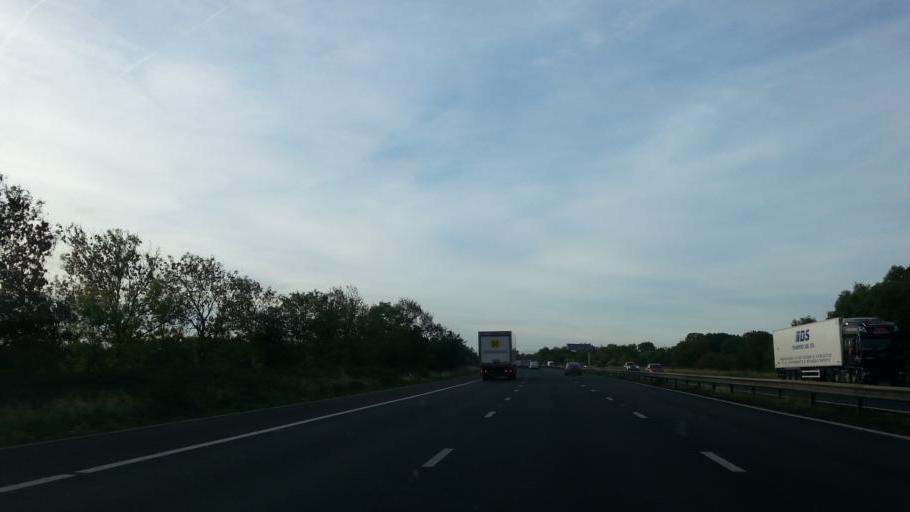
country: GB
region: England
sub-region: Leicestershire
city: Cosby
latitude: 52.5509
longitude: -1.1857
